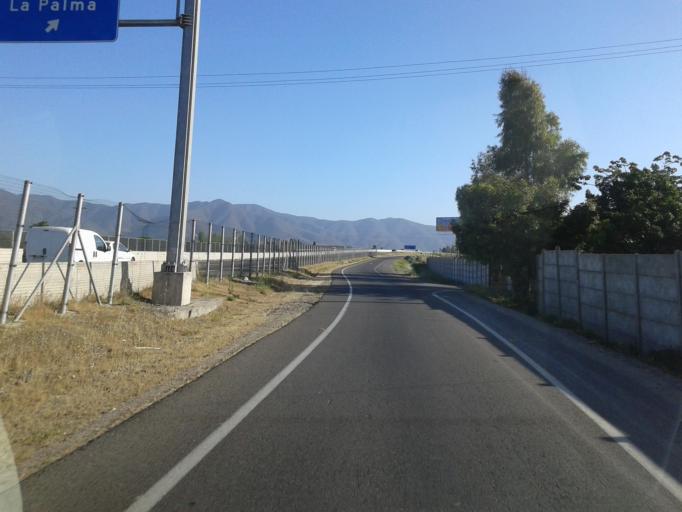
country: CL
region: Valparaiso
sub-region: Provincia de Quillota
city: Quillota
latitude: -32.8555
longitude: -71.2246
